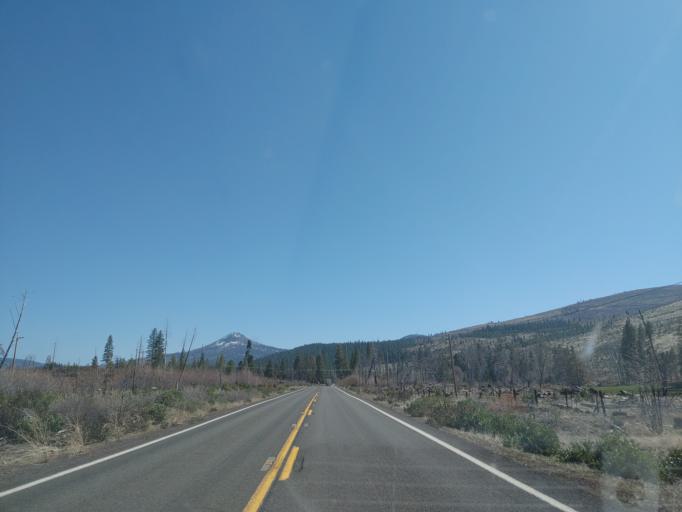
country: US
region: California
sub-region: Shasta County
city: Burney
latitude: 40.7720
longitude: -121.5018
